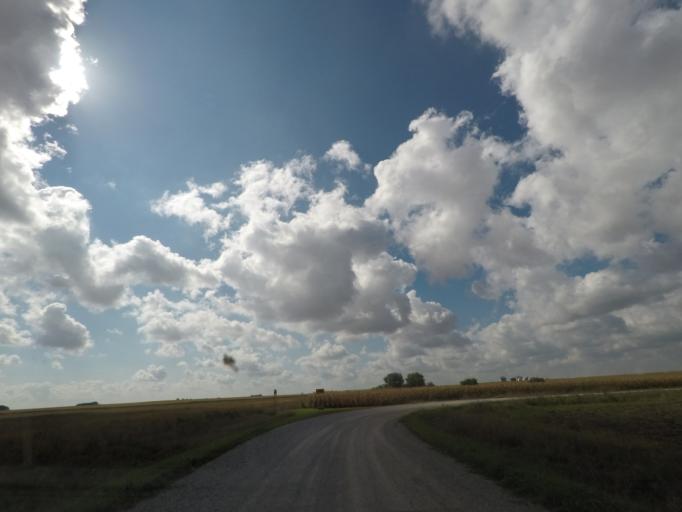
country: US
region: Iowa
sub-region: Story County
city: Nevada
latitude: 42.0012
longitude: -93.3192
